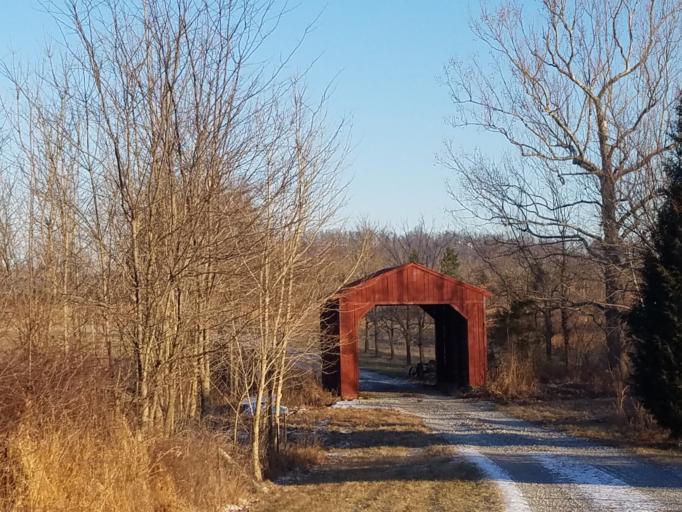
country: US
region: Kentucky
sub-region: Crittenden County
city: Marion
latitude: 37.2989
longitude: -88.0770
